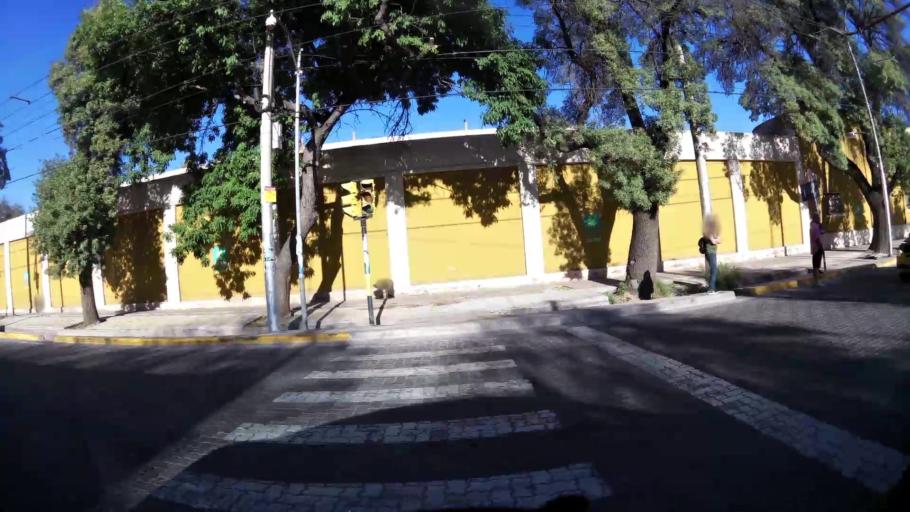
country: AR
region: Mendoza
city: Las Heras
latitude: -32.8576
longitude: -68.8334
